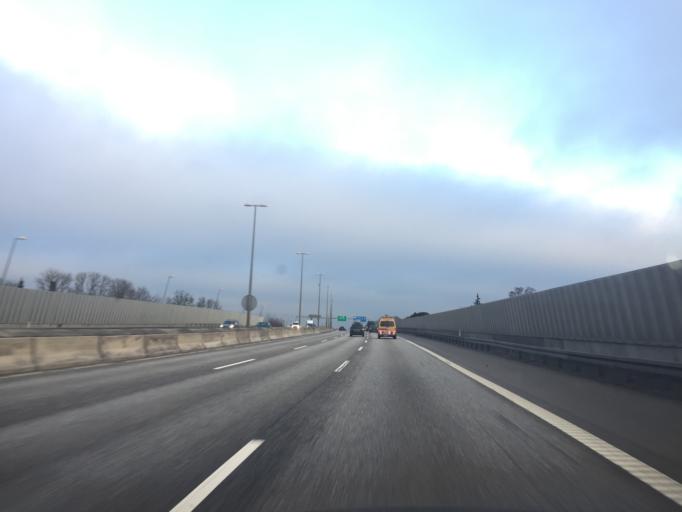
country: DK
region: Capital Region
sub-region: Herlev Kommune
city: Herlev
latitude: 55.7145
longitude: 12.4534
